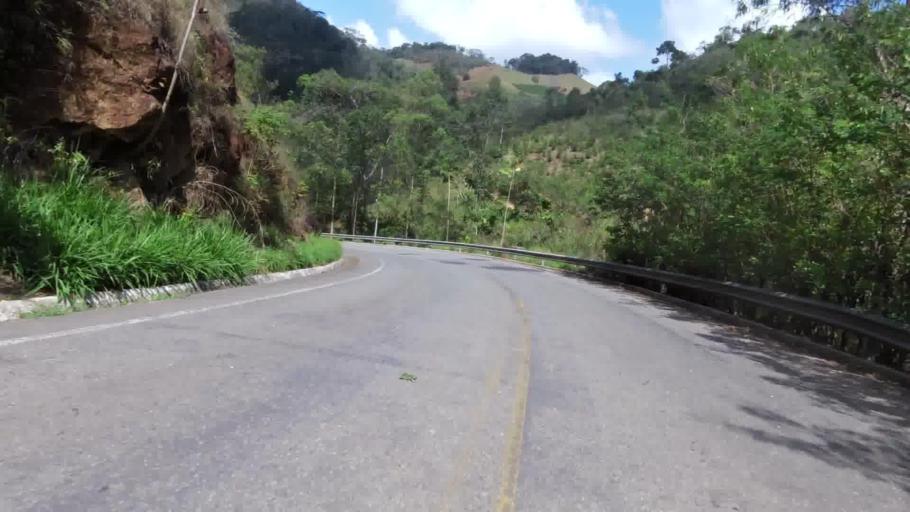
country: BR
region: Espirito Santo
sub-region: Alfredo Chaves
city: Alfredo Chaves
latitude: -20.5765
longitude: -40.8041
